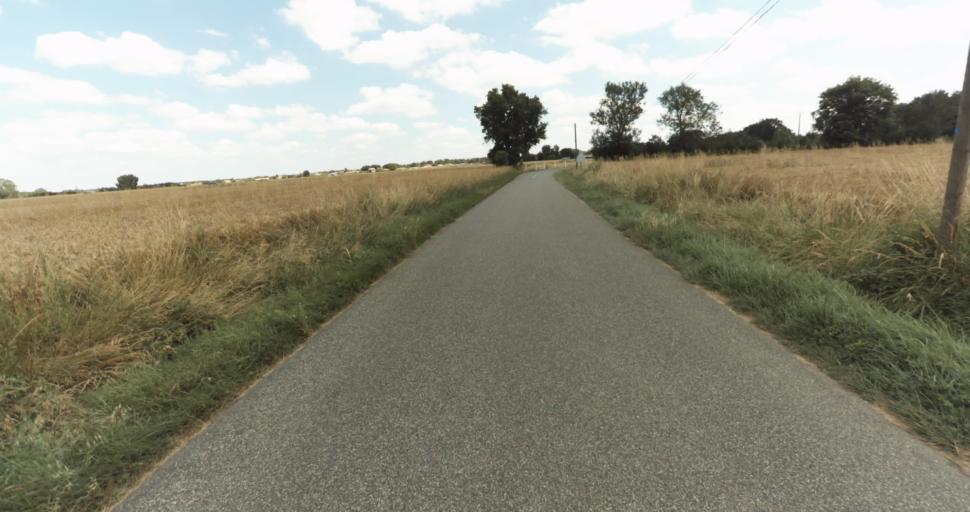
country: FR
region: Midi-Pyrenees
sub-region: Departement de la Haute-Garonne
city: Fontenilles
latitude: 43.5609
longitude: 1.1802
